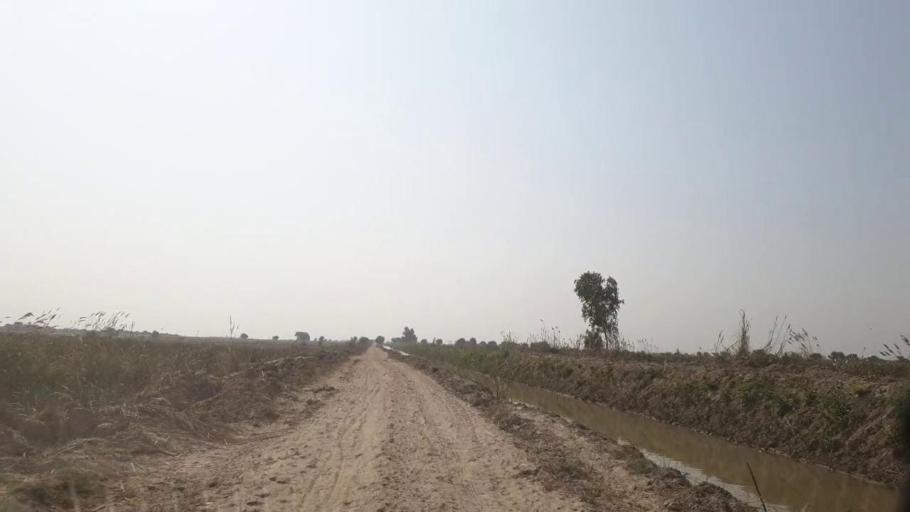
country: PK
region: Sindh
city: Bulri
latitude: 24.9801
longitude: 68.4044
